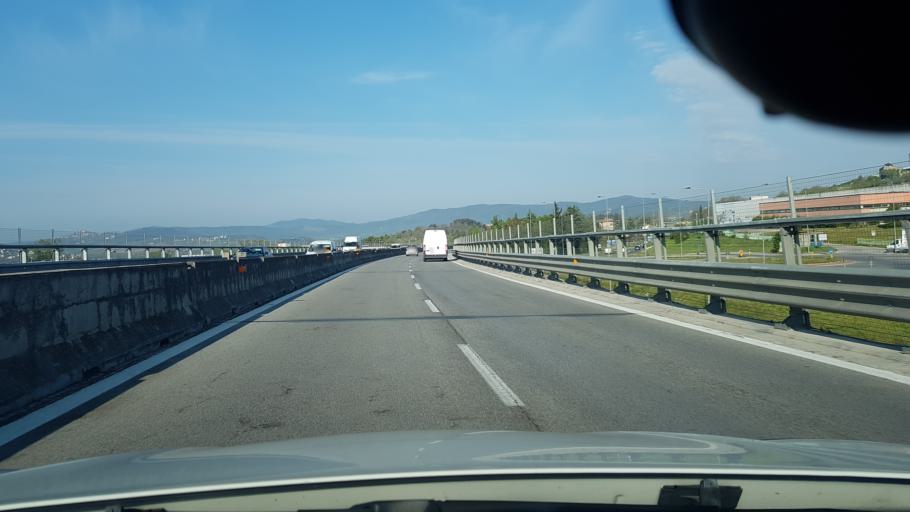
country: IT
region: Umbria
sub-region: Provincia di Perugia
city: Chiugiana-La Commenda
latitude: 43.1010
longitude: 12.3086
